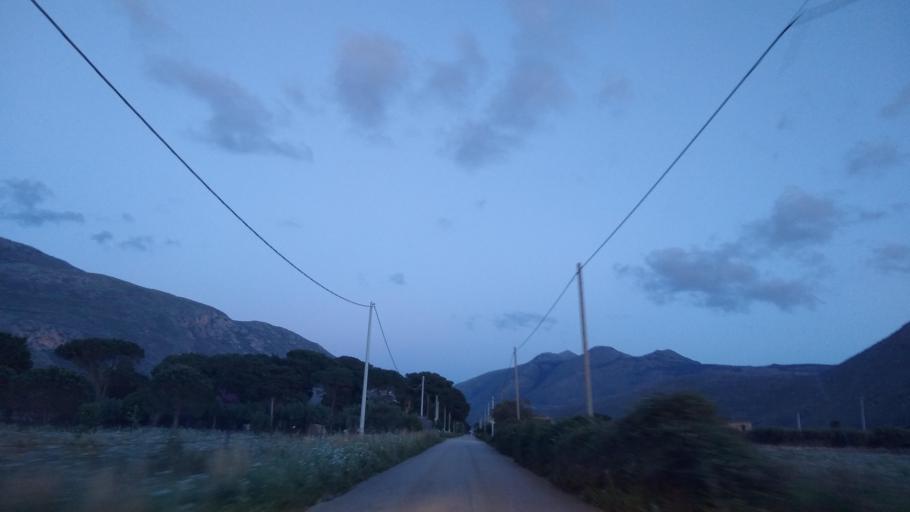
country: IT
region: Sicily
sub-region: Trapani
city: Castelluzzo
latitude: 38.1100
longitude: 12.7251
